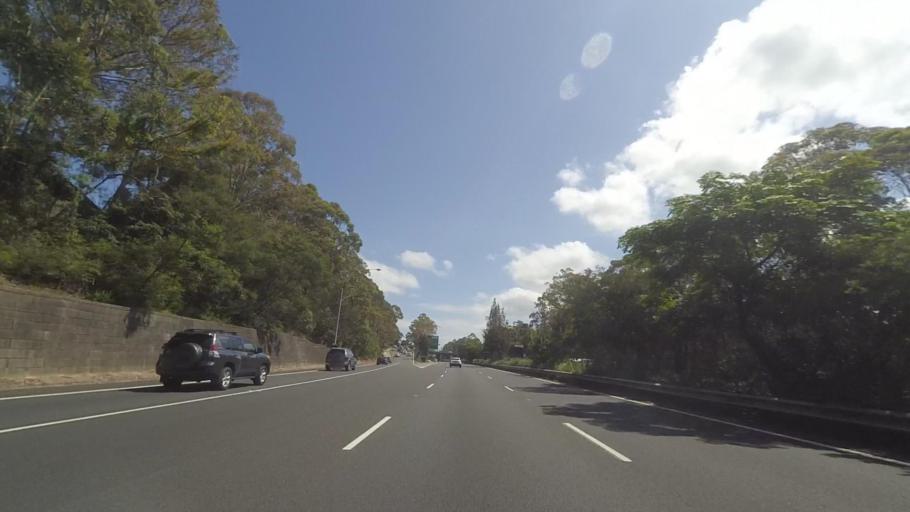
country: AU
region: New South Wales
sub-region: Ku-ring-gai
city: North Wahroonga
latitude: -33.7161
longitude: 151.1120
